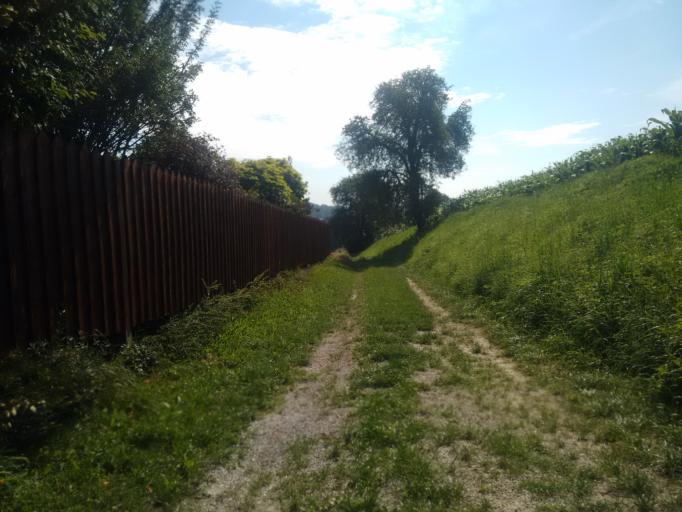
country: AT
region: Upper Austria
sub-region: Politischer Bezirk Grieskirchen
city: Bad Schallerbach
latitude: 48.1946
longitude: 13.9455
